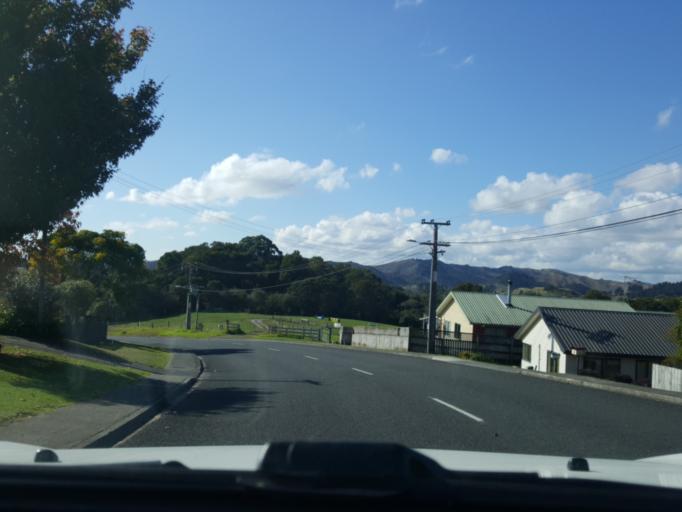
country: NZ
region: Waikato
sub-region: Waikato District
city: Ngaruawahia
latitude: -37.5418
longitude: 175.1732
